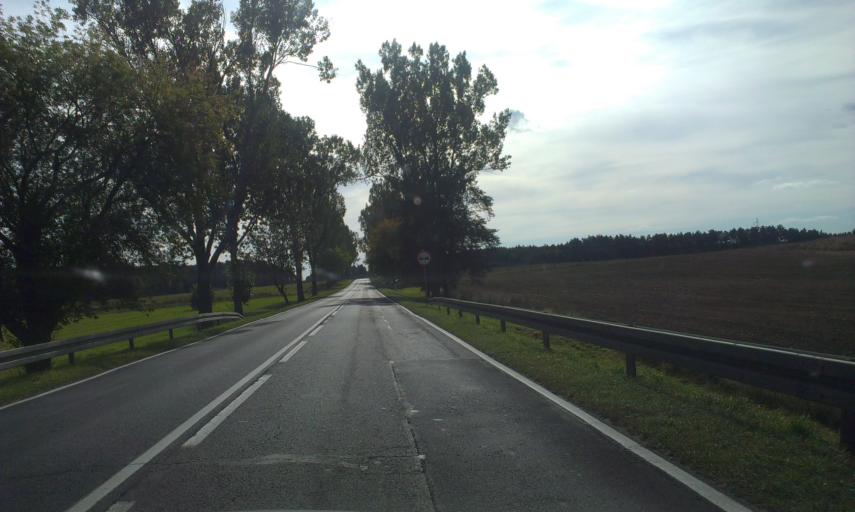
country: PL
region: Greater Poland Voivodeship
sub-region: Powiat zlotowski
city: Okonek
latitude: 53.5503
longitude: 16.8402
